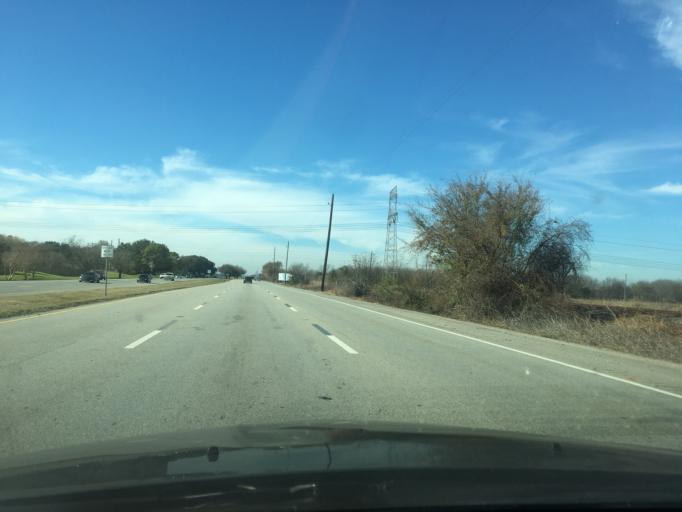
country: US
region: Texas
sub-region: Fort Bend County
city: New Territory
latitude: 29.6011
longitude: -95.6917
